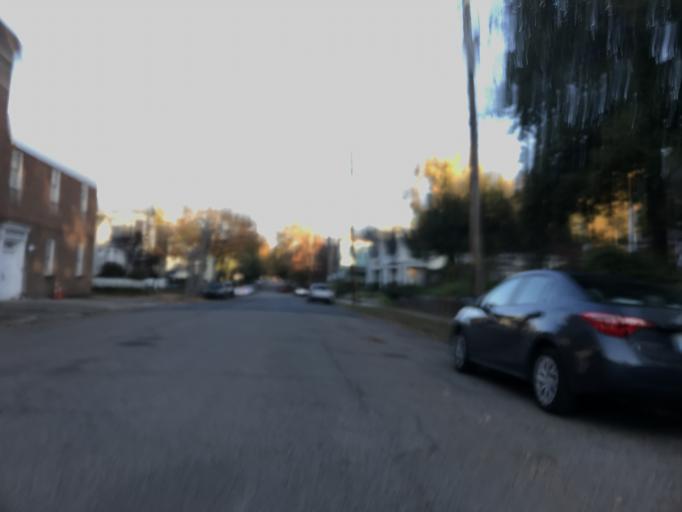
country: US
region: Kentucky
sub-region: Jefferson County
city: Audubon Park
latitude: 38.2378
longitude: -85.7269
